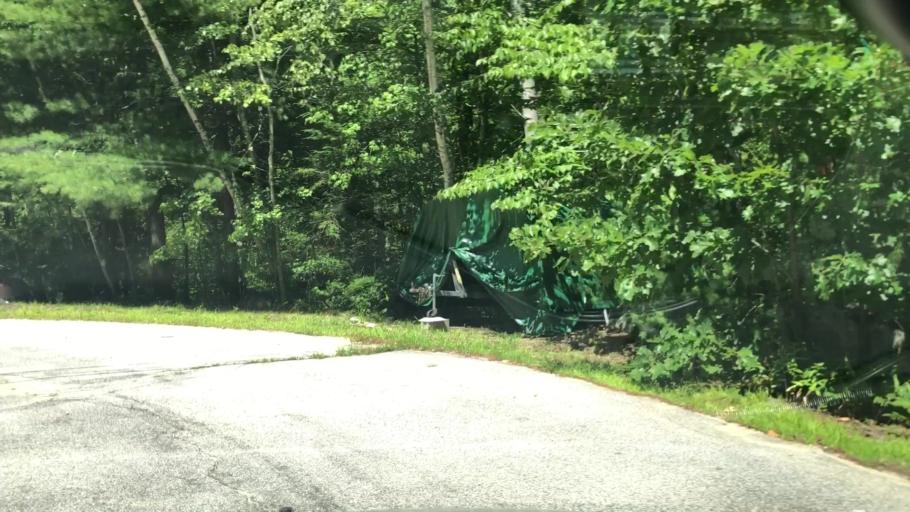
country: US
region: New Hampshire
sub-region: Hillsborough County
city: Milford
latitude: 42.8378
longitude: -71.5862
